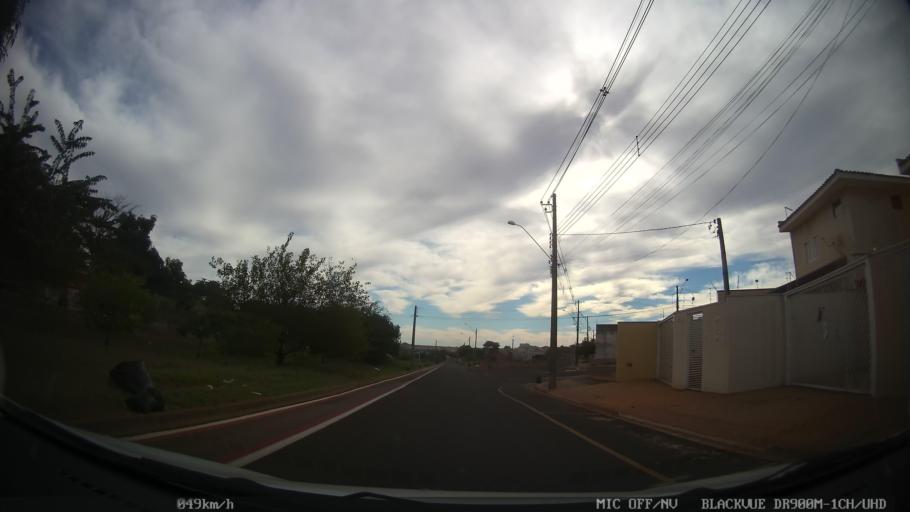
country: BR
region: Sao Paulo
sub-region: Catanduva
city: Catanduva
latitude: -21.1470
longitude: -48.9919
